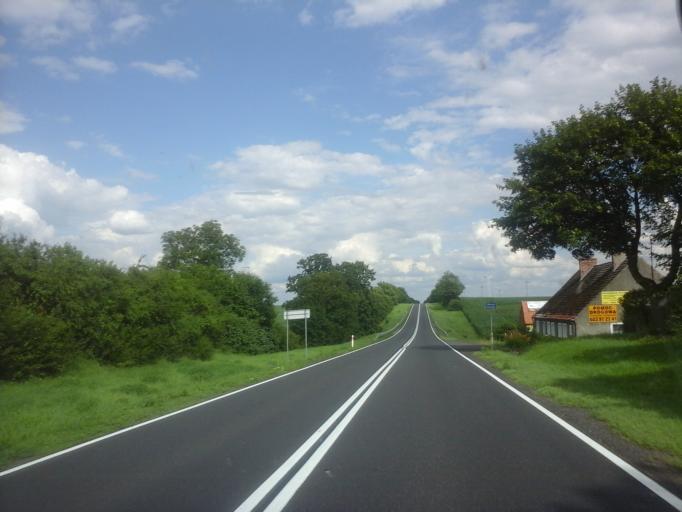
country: PL
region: West Pomeranian Voivodeship
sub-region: Powiat stargardzki
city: Dolice
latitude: 53.2945
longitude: 15.1953
